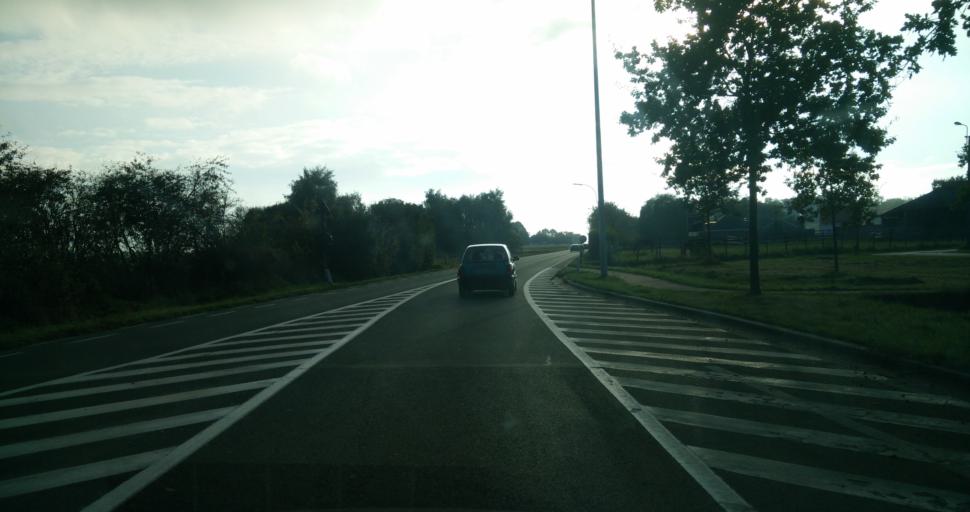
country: BE
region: Flanders
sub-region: Provincie Oost-Vlaanderen
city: Oosterzele
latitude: 50.9715
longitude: 3.8288
